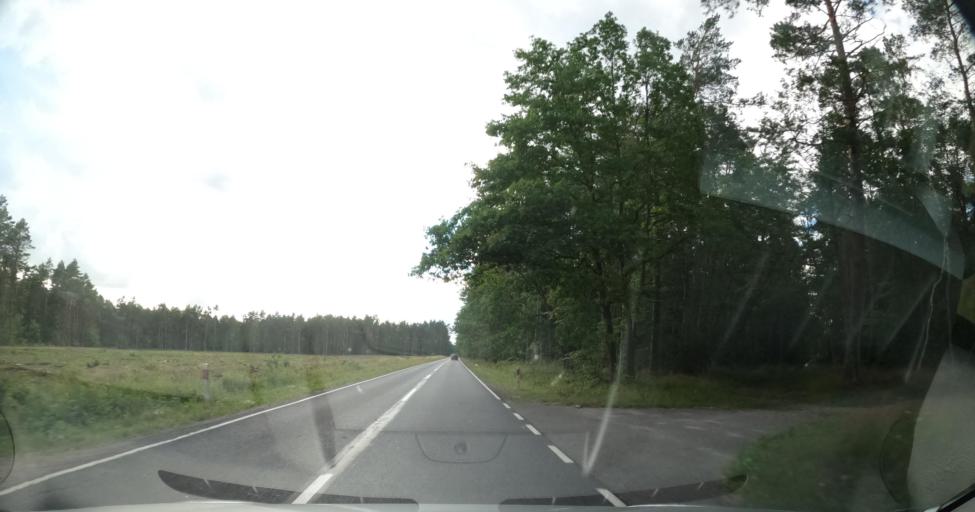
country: PL
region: Pomeranian Voivodeship
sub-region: Powiat bytowski
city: Czarna Dabrowka
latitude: 54.3847
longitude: 17.4826
